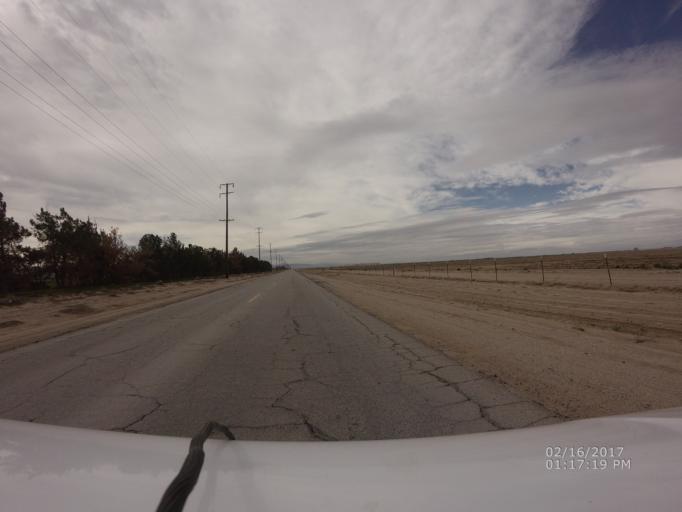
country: US
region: California
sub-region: Los Angeles County
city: Palmdale
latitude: 34.6313
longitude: -118.0274
